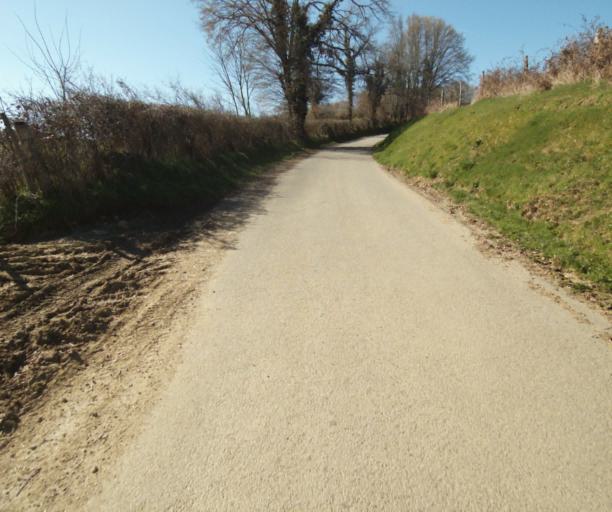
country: FR
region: Limousin
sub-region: Departement de la Correze
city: Chamboulive
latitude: 45.4218
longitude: 1.6510
